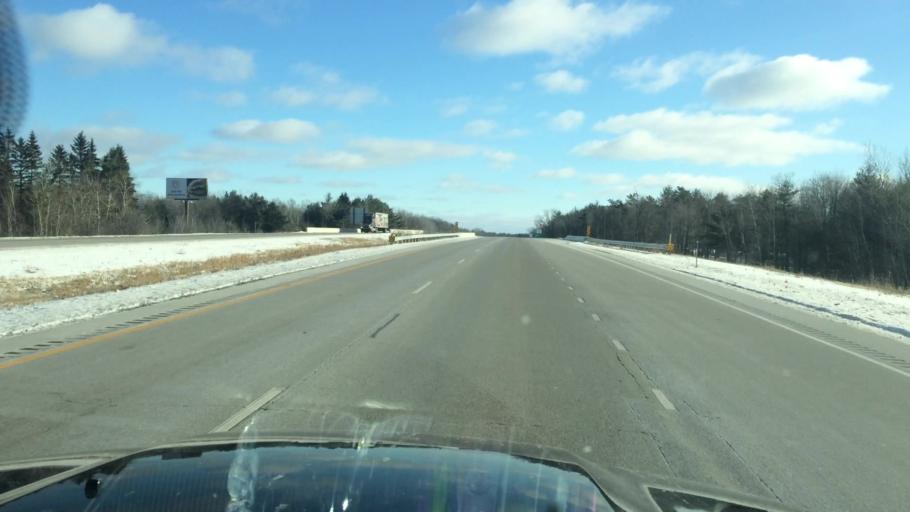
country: US
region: Wisconsin
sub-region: Portage County
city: Stevens Point
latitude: 44.5482
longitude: -89.5720
